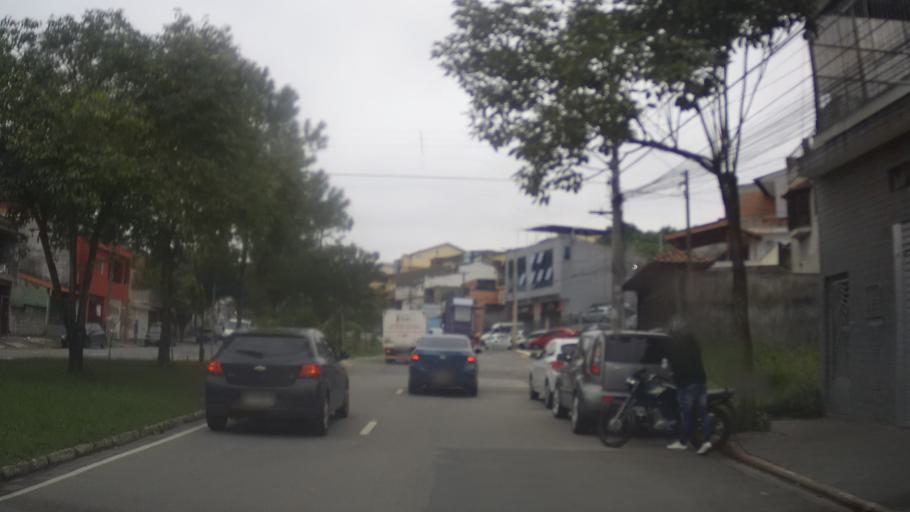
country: BR
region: Sao Paulo
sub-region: Guarulhos
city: Guarulhos
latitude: -23.4297
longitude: -46.5599
